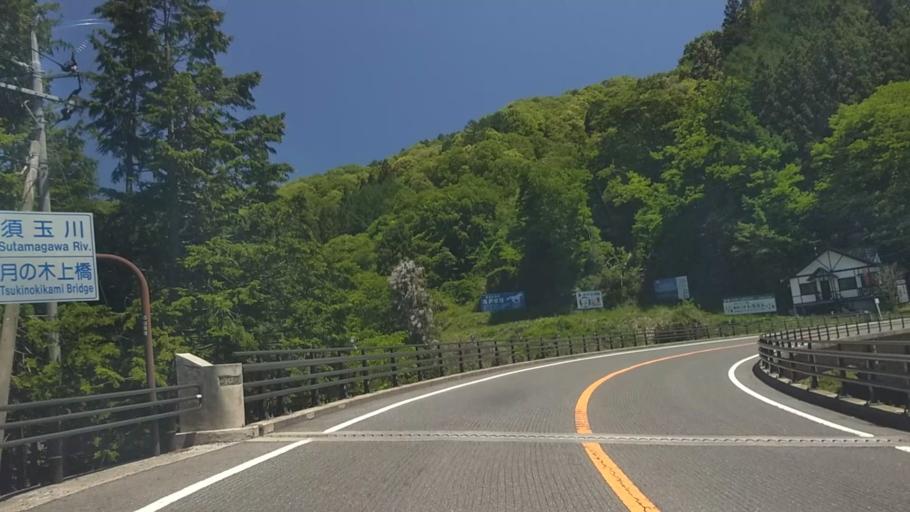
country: JP
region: Yamanashi
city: Nirasaki
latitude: 35.8848
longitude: 138.4266
